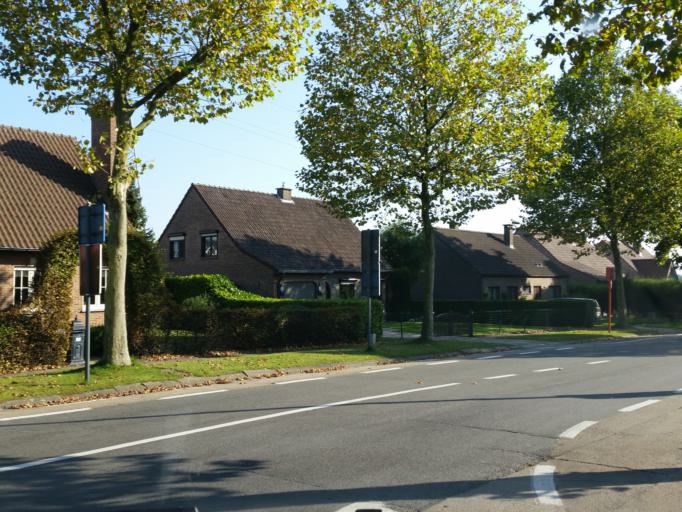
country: BE
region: Flanders
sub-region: Provincie Antwerpen
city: Rumst
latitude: 51.0907
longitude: 4.4351
